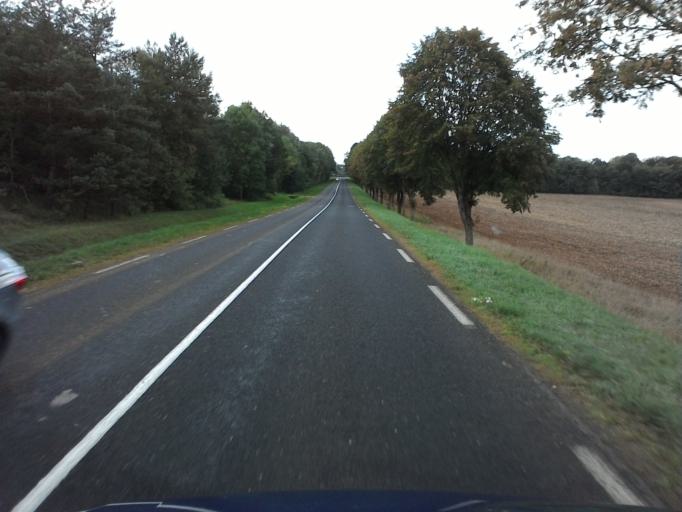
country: FR
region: Lorraine
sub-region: Departement de Meurthe-et-Moselle
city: Colombey-les-Belles
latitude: 48.5039
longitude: 5.8771
